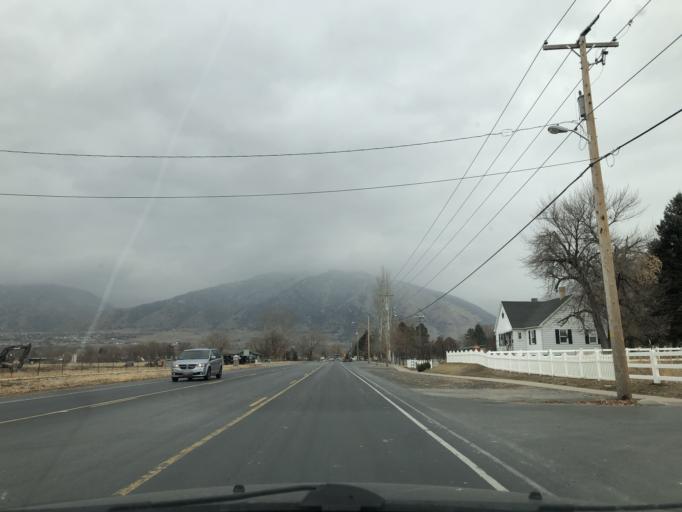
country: US
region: Utah
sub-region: Cache County
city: Nibley
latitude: 41.6747
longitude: -111.8424
